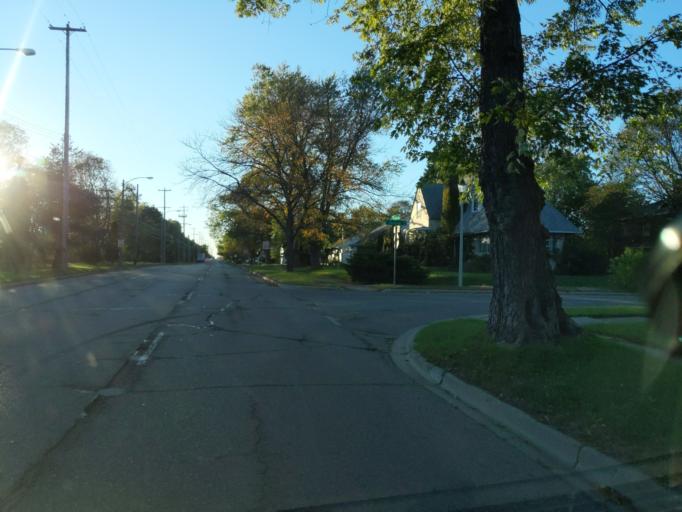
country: US
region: Michigan
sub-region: Ingham County
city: Lansing
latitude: 42.7265
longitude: -84.5725
